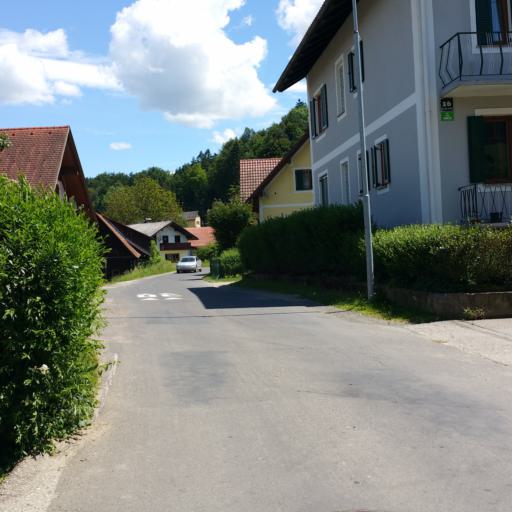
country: AT
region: Styria
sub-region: Politischer Bezirk Leibnitz
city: Gleinstatten
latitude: 46.7395
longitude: 15.3611
